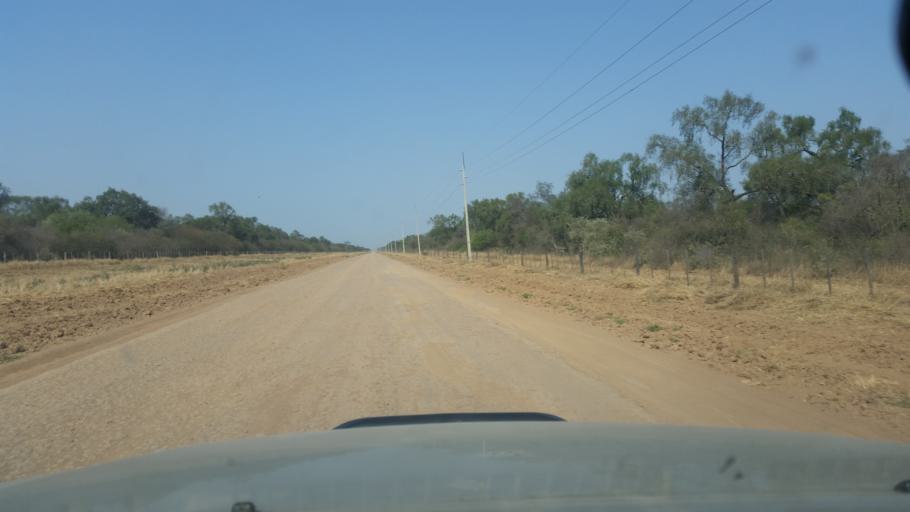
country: PY
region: Boqueron
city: Filadelfia
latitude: -22.0746
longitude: -60.7605
